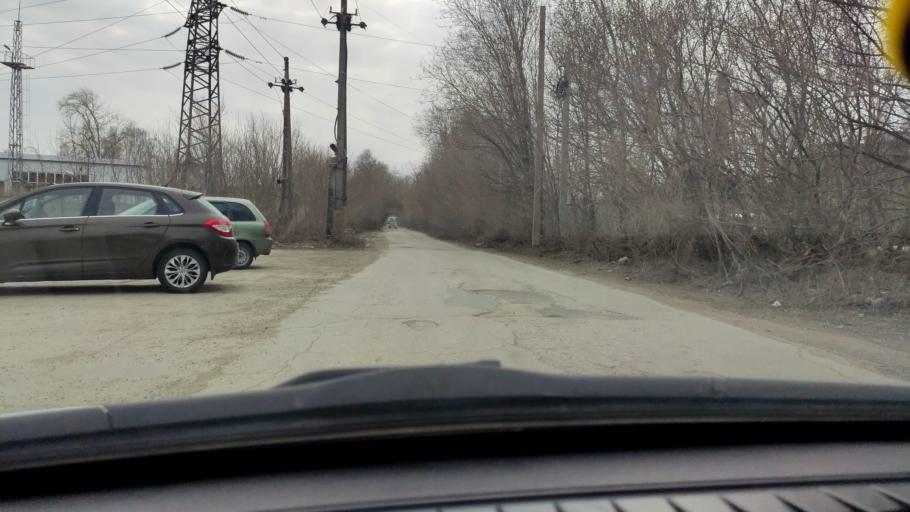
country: RU
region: Samara
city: Tol'yatti
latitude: 53.5221
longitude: 49.4550
